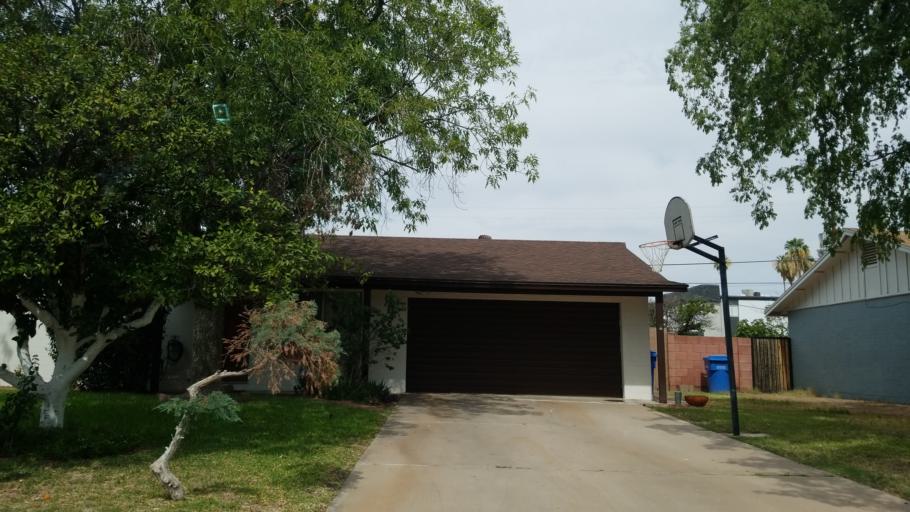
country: US
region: Arizona
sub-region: Maricopa County
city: Glendale
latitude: 33.5481
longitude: -112.0981
